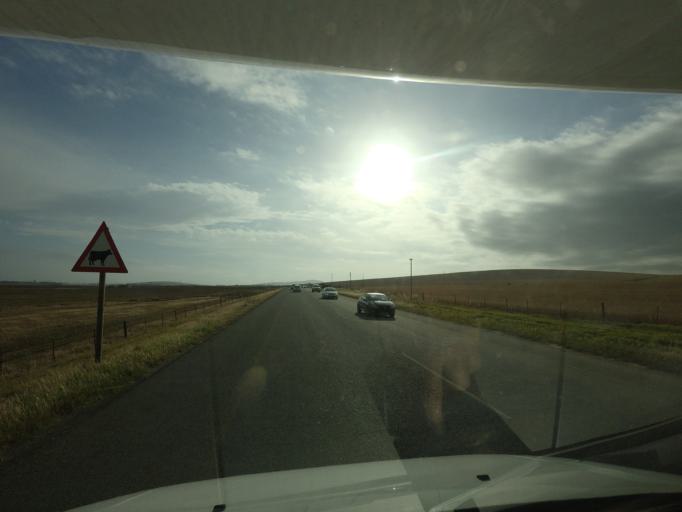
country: ZA
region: Western Cape
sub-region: City of Cape Town
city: Sunset Beach
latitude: -33.7257
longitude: 18.4884
